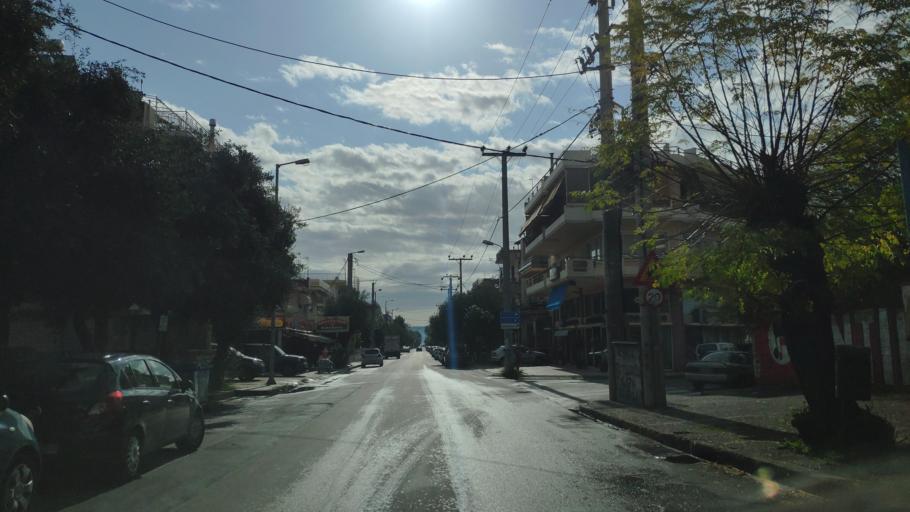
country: GR
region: Attica
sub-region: Nomarchia Dytikis Attikis
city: Elefsina
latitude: 38.0440
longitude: 23.5444
